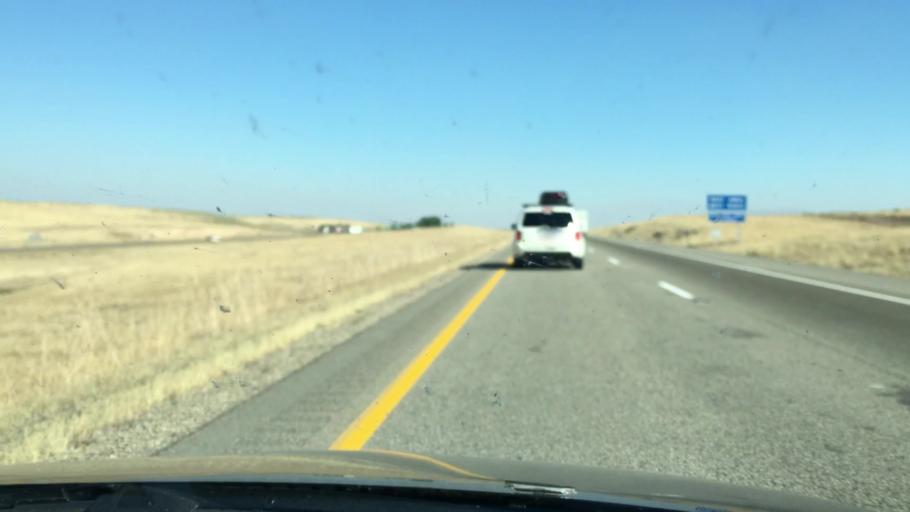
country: US
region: Idaho
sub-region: Ada County
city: Boise
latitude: 43.4837
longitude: -116.1157
